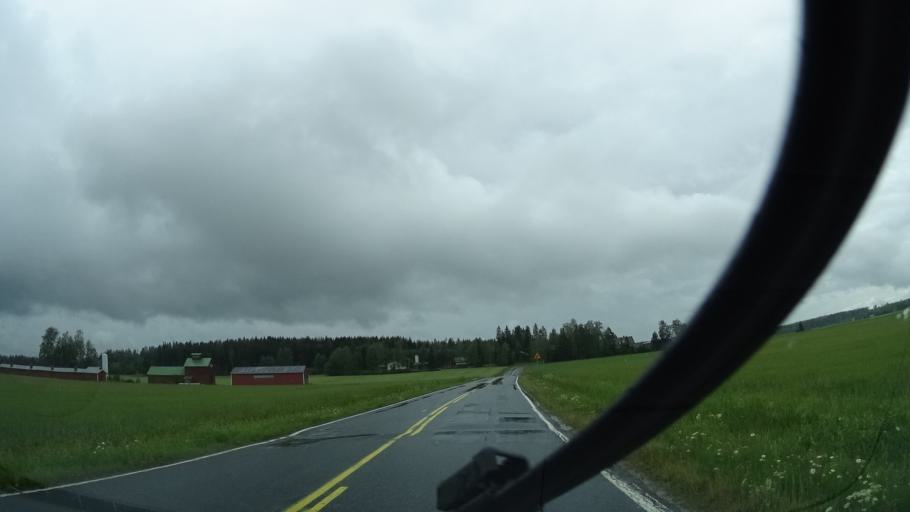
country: FI
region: Haeme
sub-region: Forssa
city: Humppila
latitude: 61.0019
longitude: 23.2516
